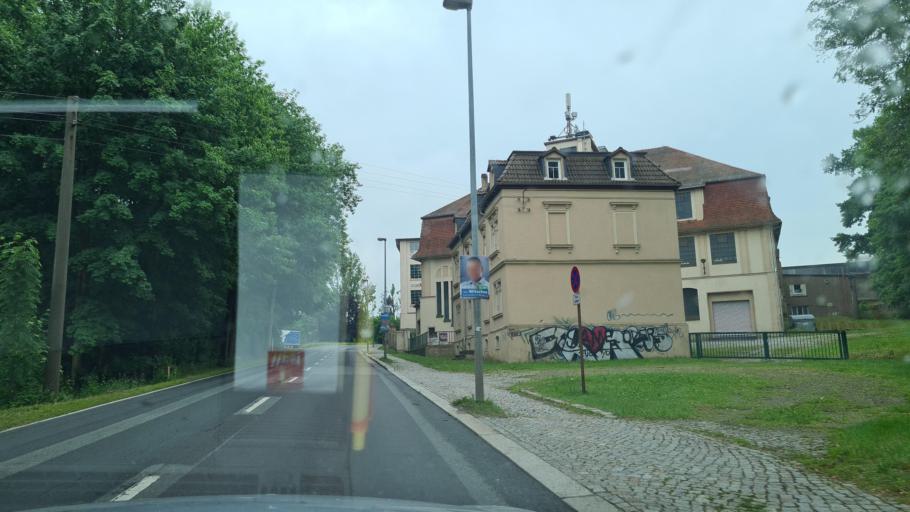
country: DE
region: Saxony
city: Kirschau
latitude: 51.0891
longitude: 14.4262
